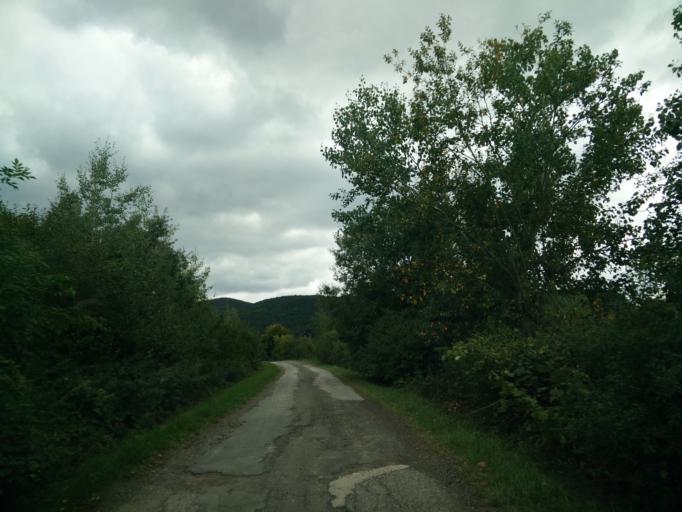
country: SK
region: Nitriansky
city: Novaky
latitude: 48.6332
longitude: 18.4991
